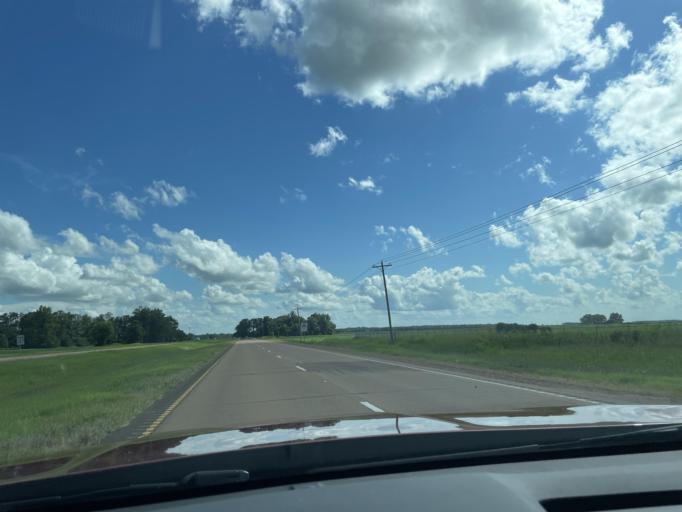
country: US
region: Mississippi
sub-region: Humphreys County
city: Belzoni
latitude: 33.1429
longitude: -90.5134
